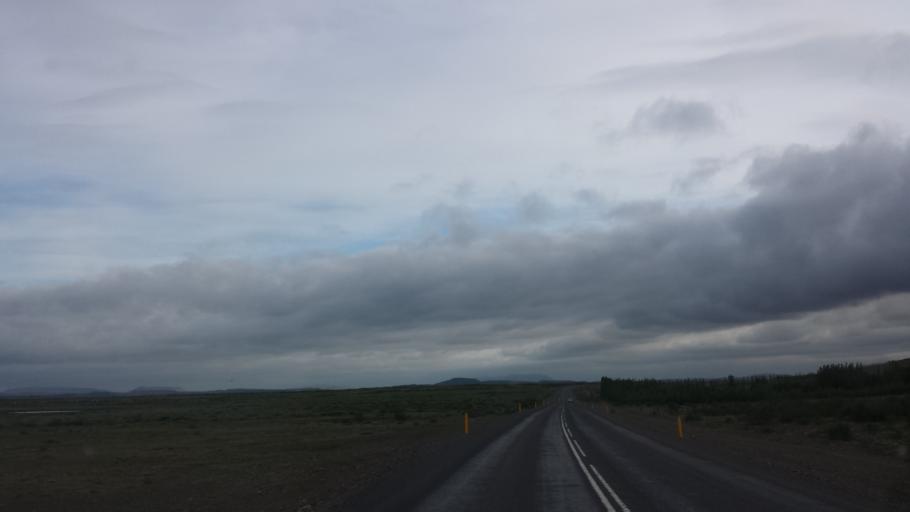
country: IS
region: South
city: Selfoss
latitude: 64.2845
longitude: -20.3414
